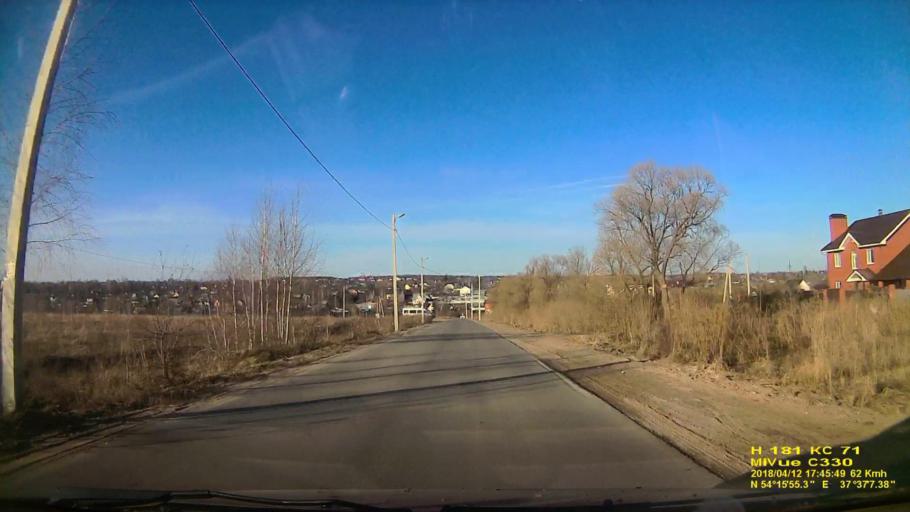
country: RU
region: Tula
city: Gorelki
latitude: 54.2655
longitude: 37.6189
